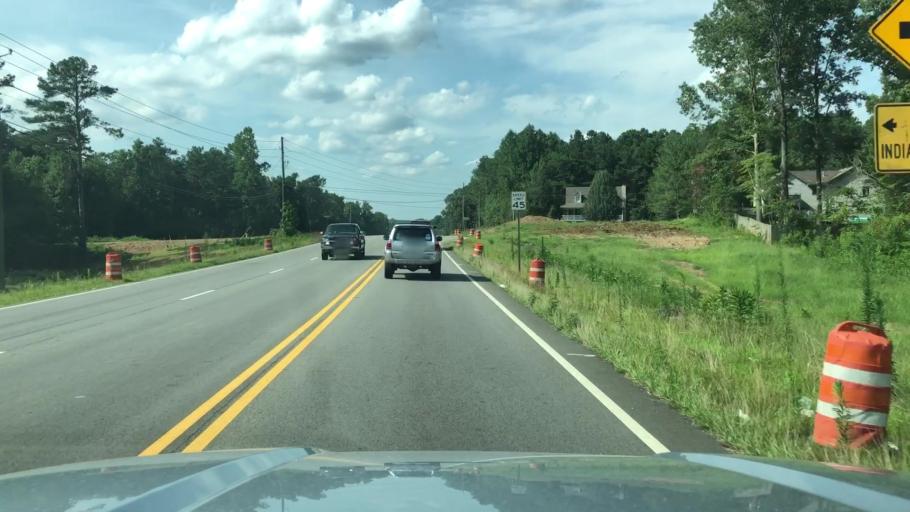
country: US
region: Georgia
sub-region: Douglas County
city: Douglasville
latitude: 33.8043
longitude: -84.7581
